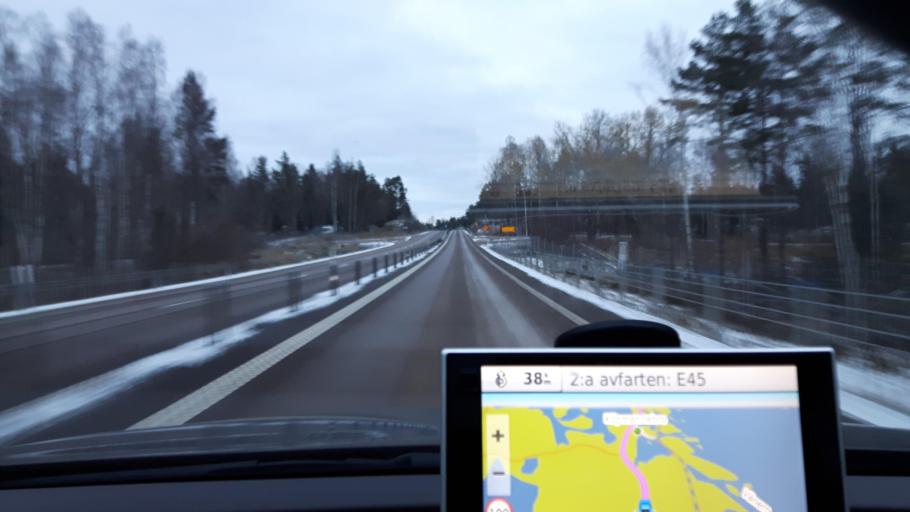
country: SE
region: Vaestra Goetaland
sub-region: Melleruds Kommun
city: Mellerud
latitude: 58.7514
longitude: 12.4855
